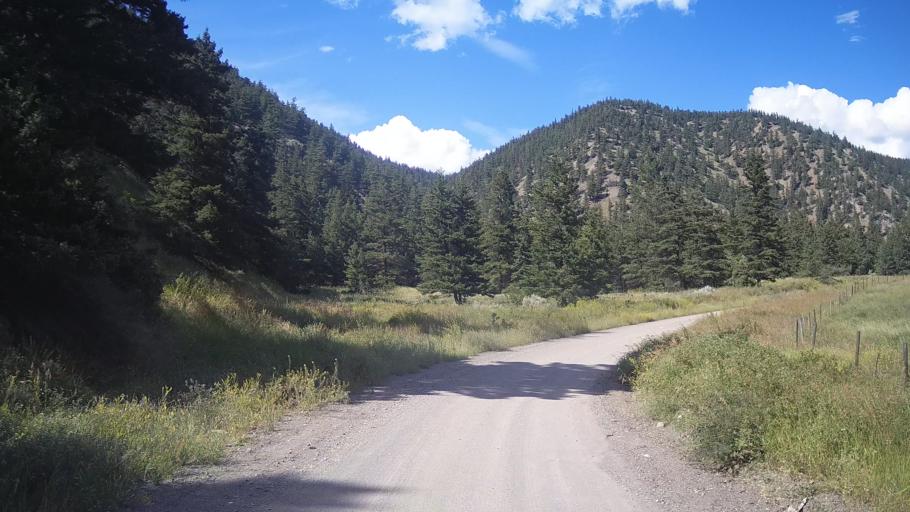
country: CA
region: British Columbia
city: Lillooet
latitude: 51.2476
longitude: -122.0276
